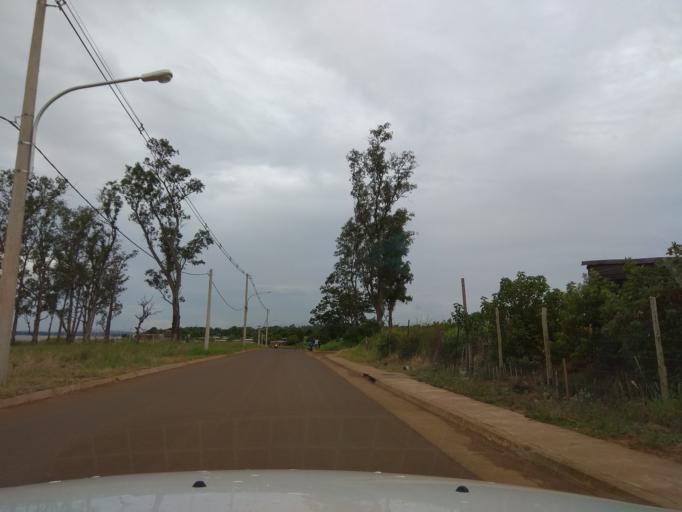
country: AR
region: Misiones
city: Garupa
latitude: -27.4342
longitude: -55.8645
